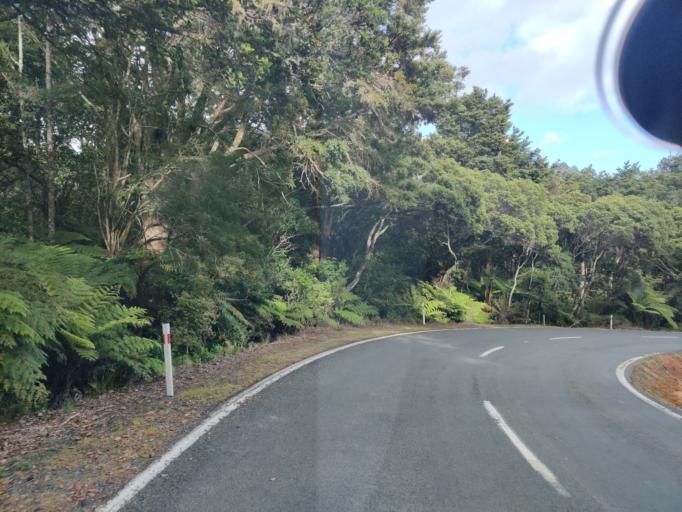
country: NZ
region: Northland
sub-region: Whangarei
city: Ngunguru
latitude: -35.5828
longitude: 174.4259
